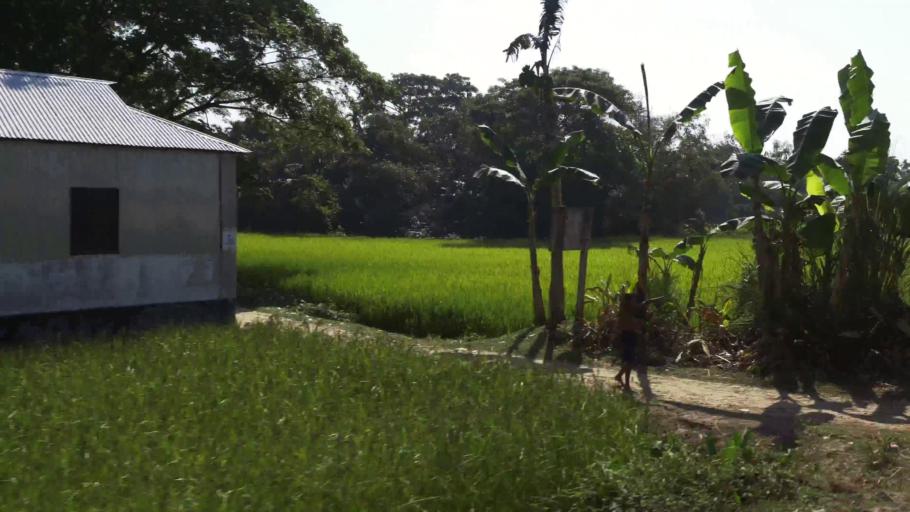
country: BD
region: Dhaka
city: Gafargaon
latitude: 24.5598
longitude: 90.5084
